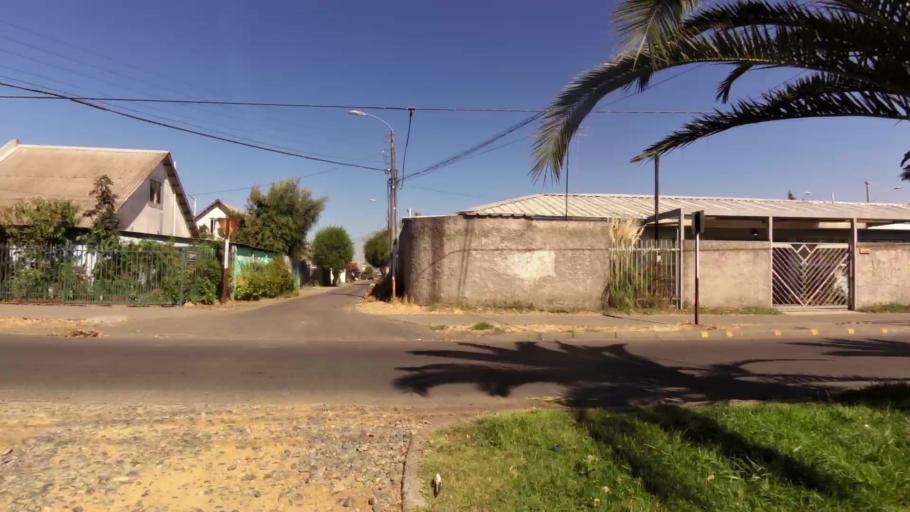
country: CL
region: Maule
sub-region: Provincia de Curico
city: Curico
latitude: -34.9783
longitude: -71.2530
